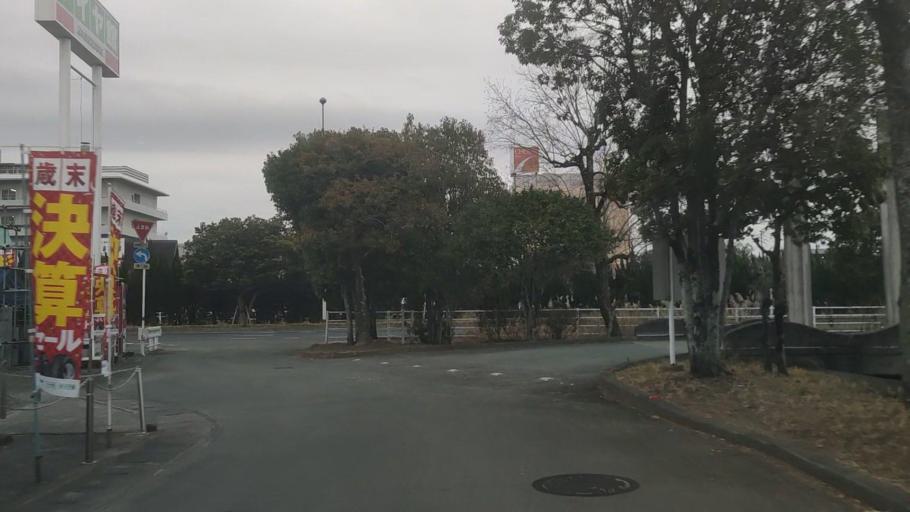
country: JP
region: Kumamoto
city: Kumamoto
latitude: 32.7645
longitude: 130.7090
